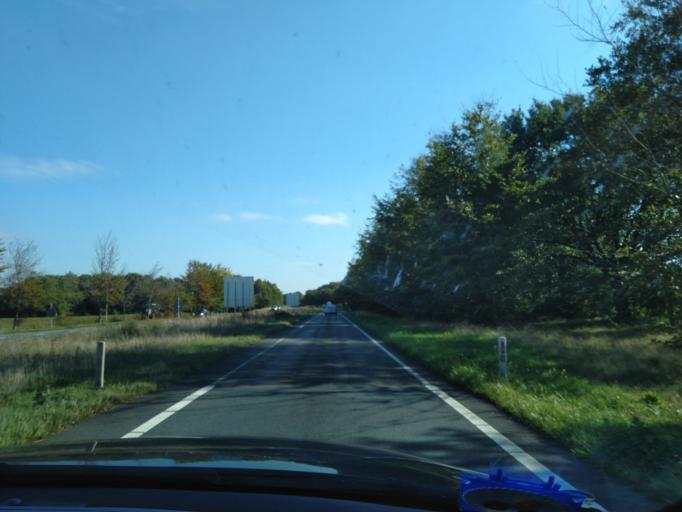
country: NL
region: Groningen
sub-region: Gemeente Veendam
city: Veendam
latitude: 53.0964
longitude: 6.9011
